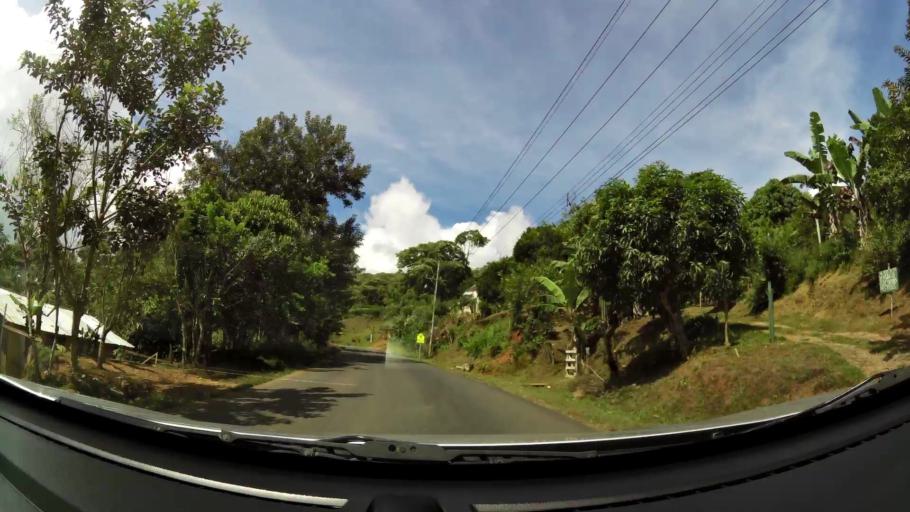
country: CR
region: San Jose
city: San Isidro
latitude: 9.3263
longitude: -83.7431
